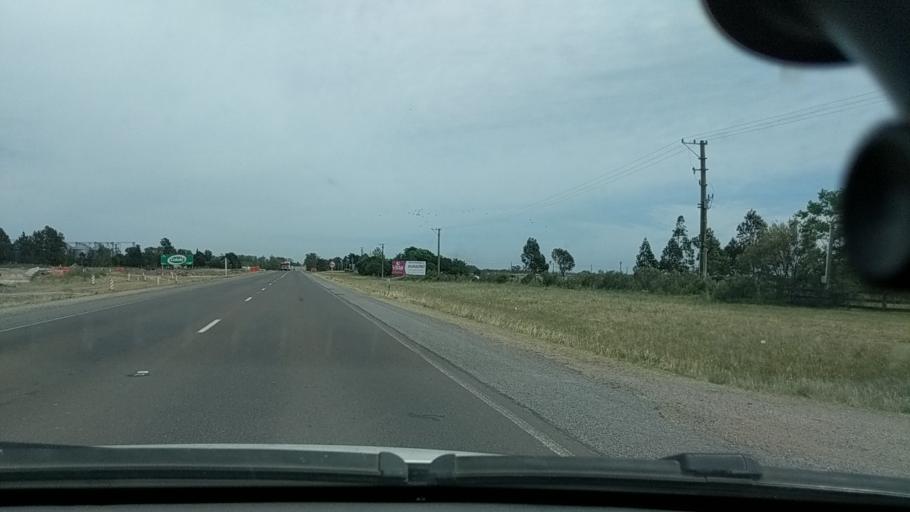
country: UY
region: Durazno
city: Durazno
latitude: -33.4424
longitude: -56.4809
